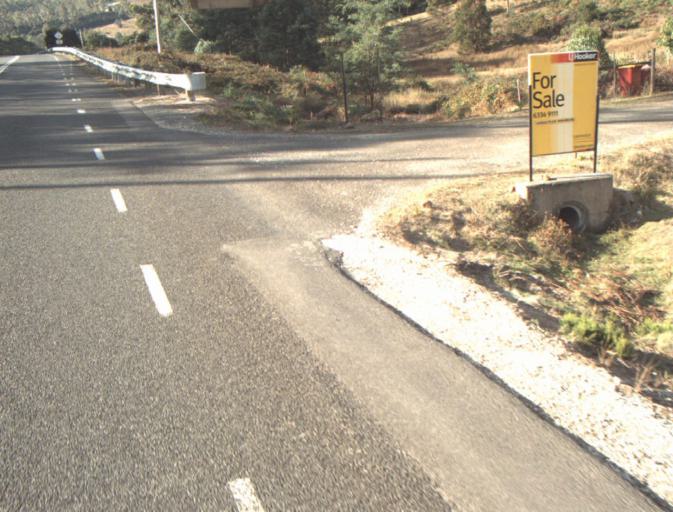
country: AU
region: Tasmania
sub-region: Launceston
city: Mayfield
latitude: -41.2857
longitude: 147.2182
